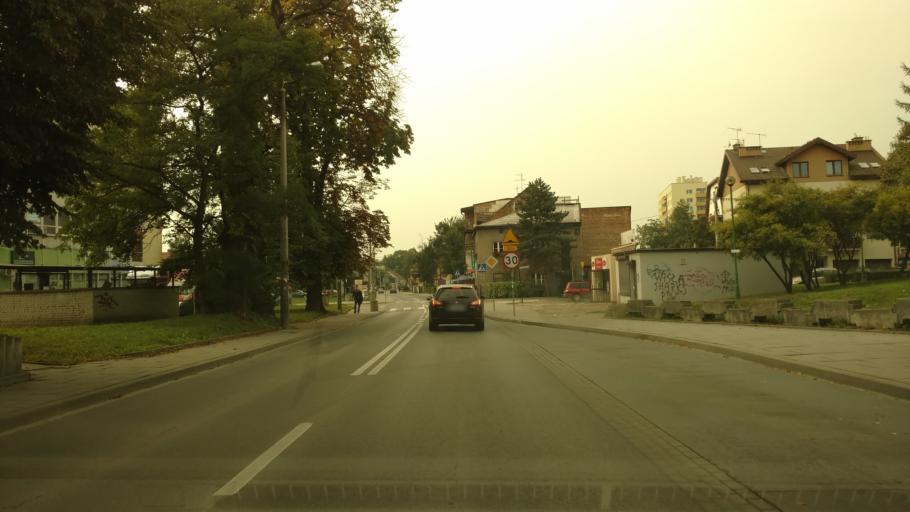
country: PL
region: Lesser Poland Voivodeship
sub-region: Krakow
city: Krakow
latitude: 50.0886
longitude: 19.9686
